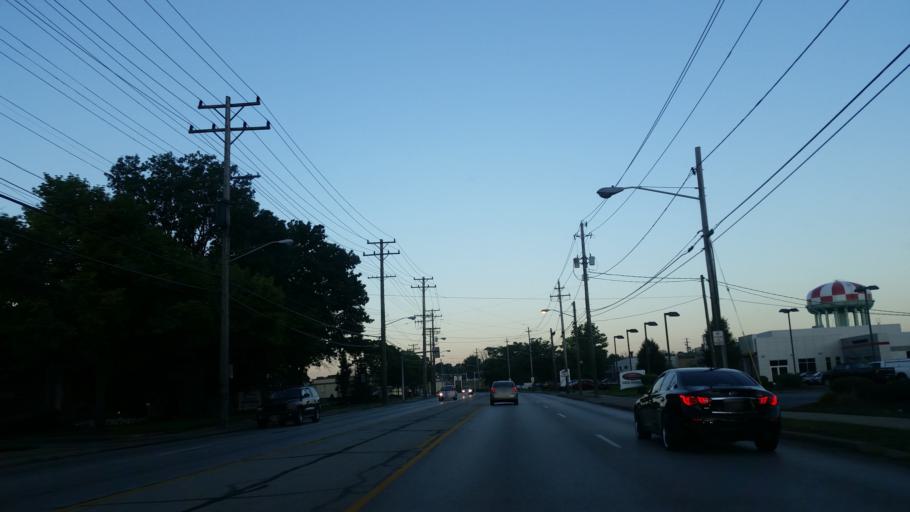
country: US
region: Ohio
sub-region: Cuyahoga County
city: North Olmsted
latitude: 41.4180
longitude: -81.9186
